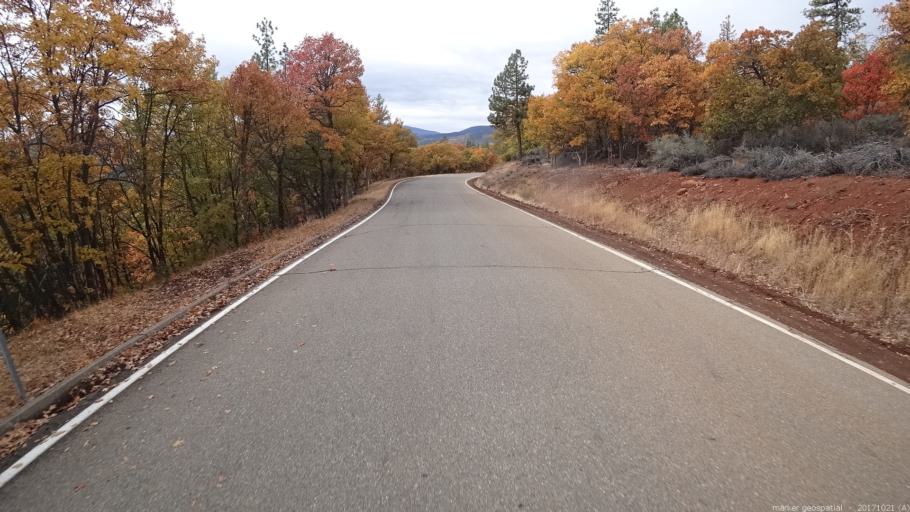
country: US
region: California
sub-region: Shasta County
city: Burney
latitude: 41.0412
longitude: -121.6499
